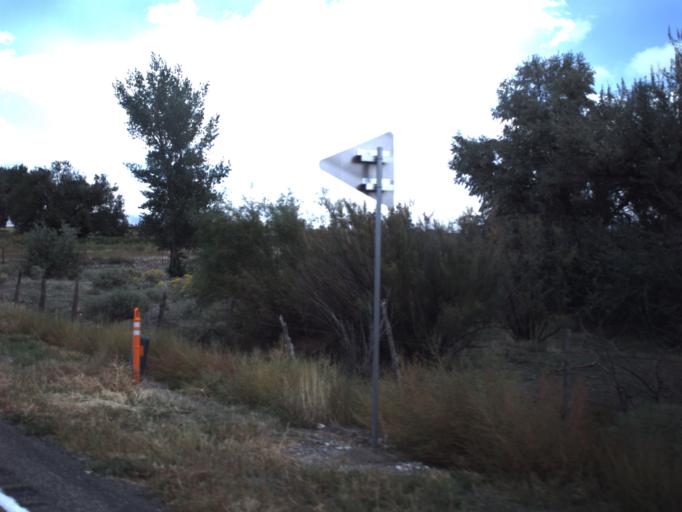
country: US
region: Utah
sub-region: Sevier County
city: Monroe
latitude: 38.6760
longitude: -112.1211
